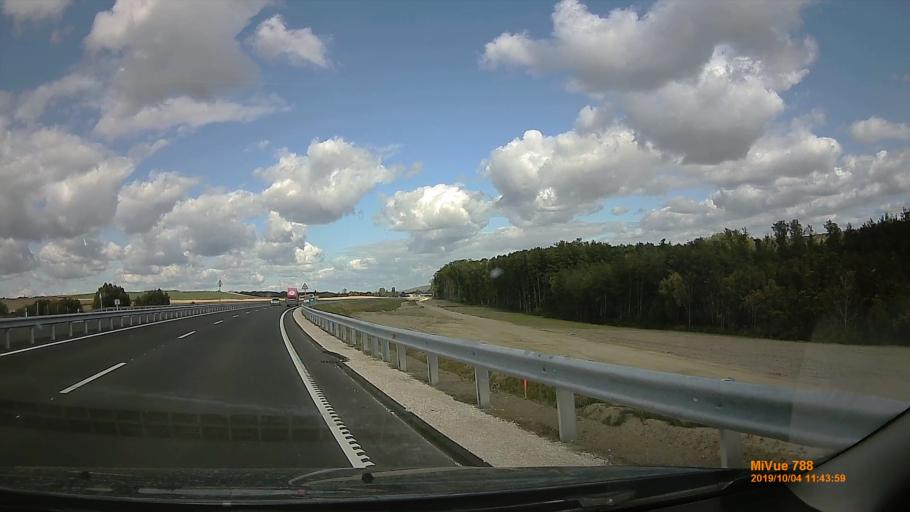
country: HU
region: Somogy
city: Karad
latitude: 46.6075
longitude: 17.7986
